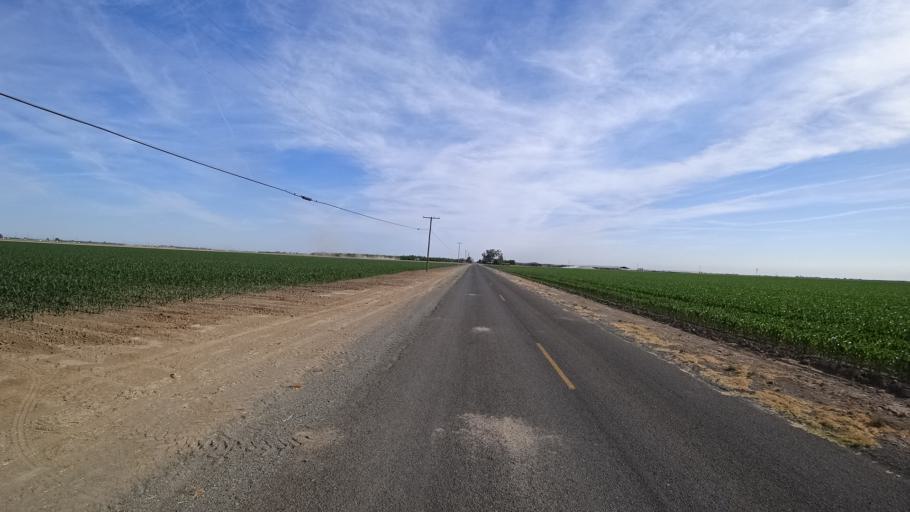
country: US
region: California
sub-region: Kings County
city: Home Garden
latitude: 36.3465
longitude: -119.5471
